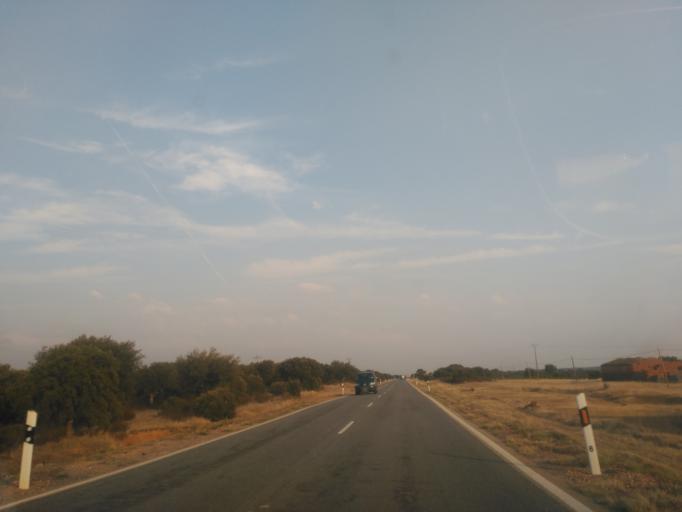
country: ES
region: Castille and Leon
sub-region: Provincia de Zamora
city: Perilla de Castro
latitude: 41.7268
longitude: -5.8178
